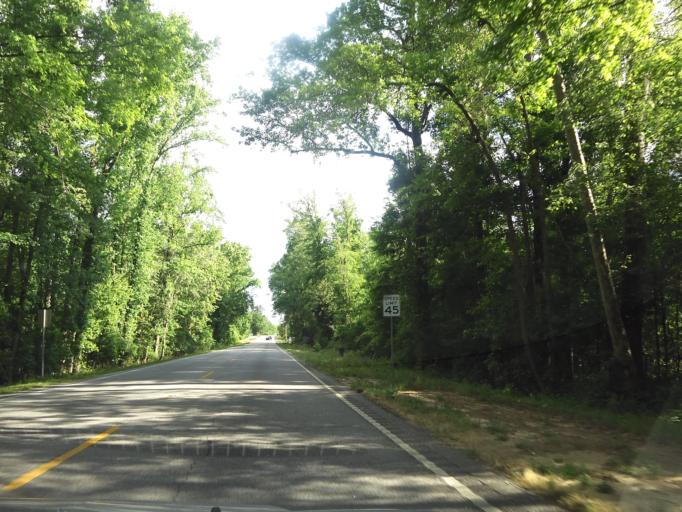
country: US
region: South Carolina
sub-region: Allendale County
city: Fairfax
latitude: 32.8674
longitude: -81.2381
